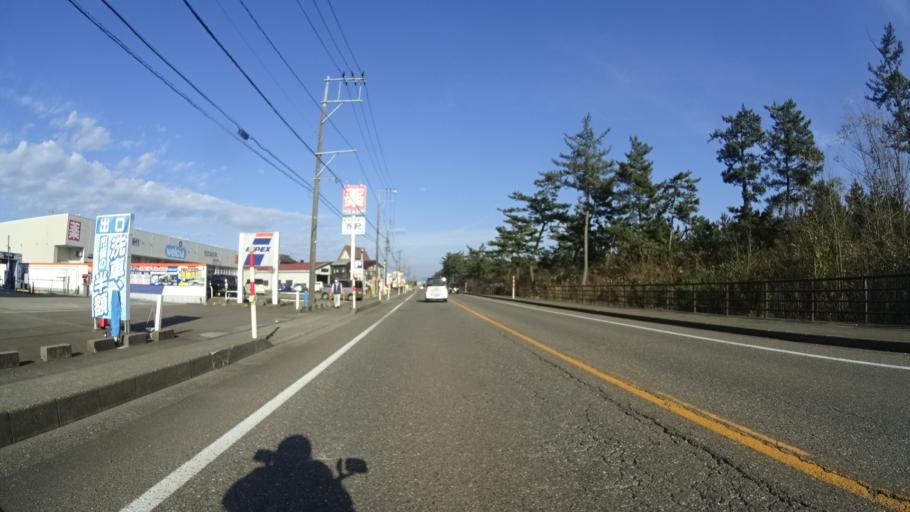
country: JP
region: Niigata
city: Joetsu
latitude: 37.2207
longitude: 138.3206
